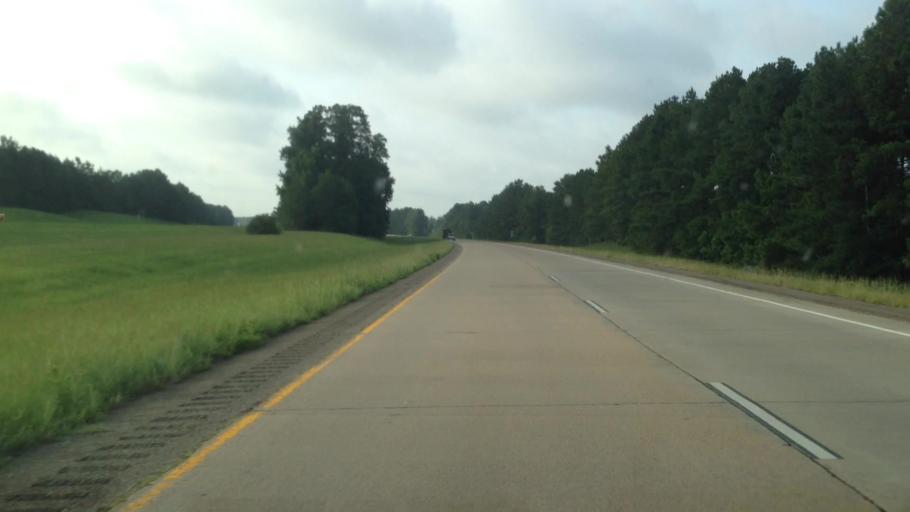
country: US
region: Louisiana
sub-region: Rapides Parish
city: Lecompte
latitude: 31.0375
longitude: -92.4145
